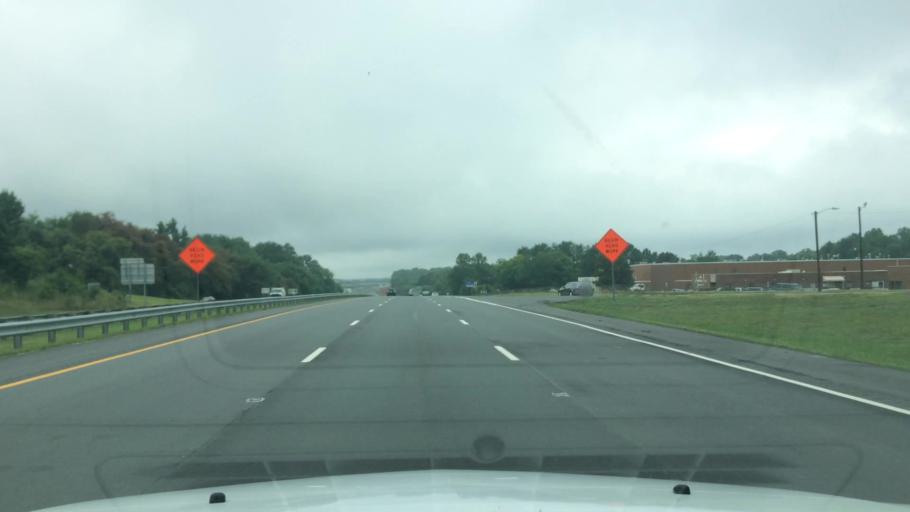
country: US
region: North Carolina
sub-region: Forsyth County
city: Clemmons
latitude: 36.0727
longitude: -80.3401
